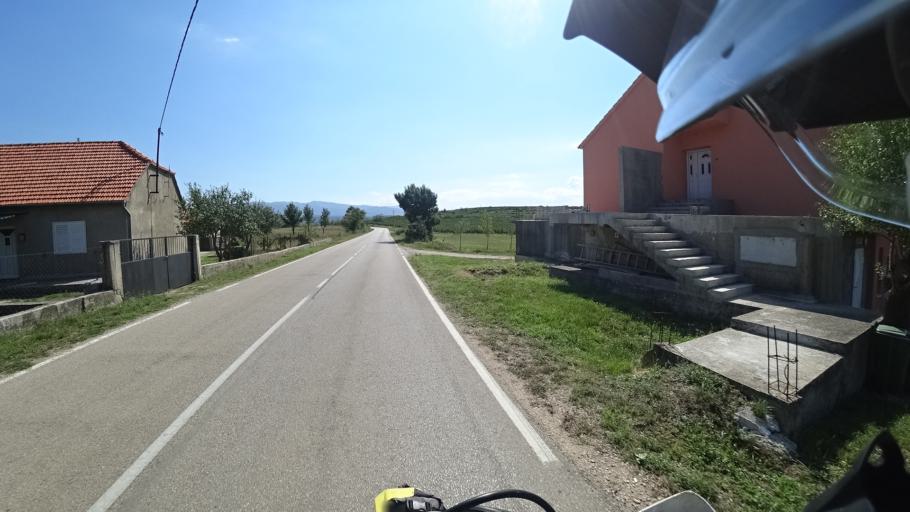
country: HR
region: Sibensko-Kniniska
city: Drnis
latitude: 43.8664
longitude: 16.1903
